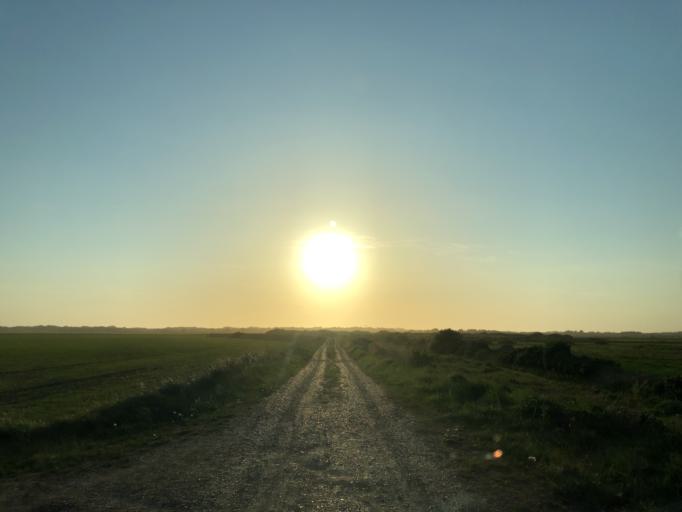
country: DK
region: Central Jutland
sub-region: Holstebro Kommune
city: Ulfborg
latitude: 56.2471
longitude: 8.1610
